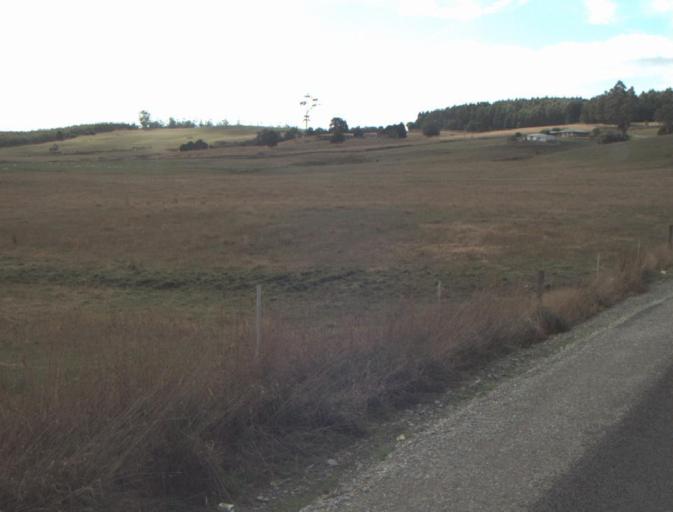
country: AU
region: Tasmania
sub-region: Launceston
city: Mayfield
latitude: -41.1975
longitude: 147.1808
